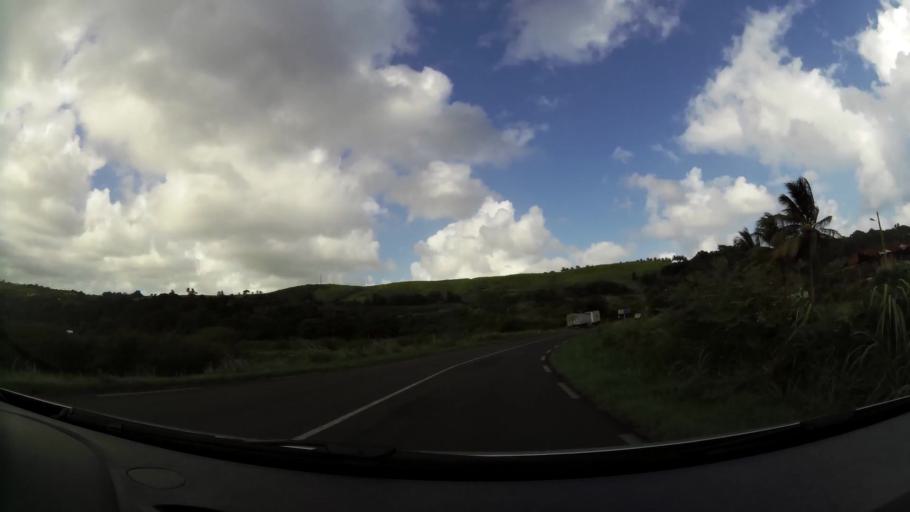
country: MQ
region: Martinique
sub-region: Martinique
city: Le Lorrain
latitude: 14.8255
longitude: -61.0415
